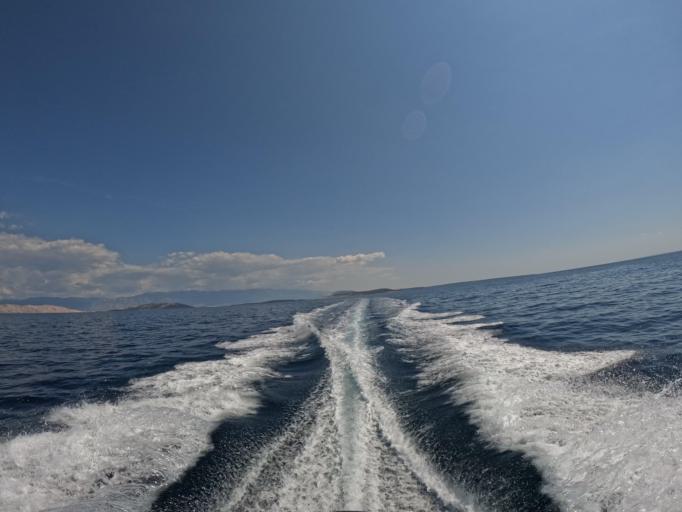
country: HR
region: Primorsko-Goranska
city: Lopar
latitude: 44.8869
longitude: 14.6400
